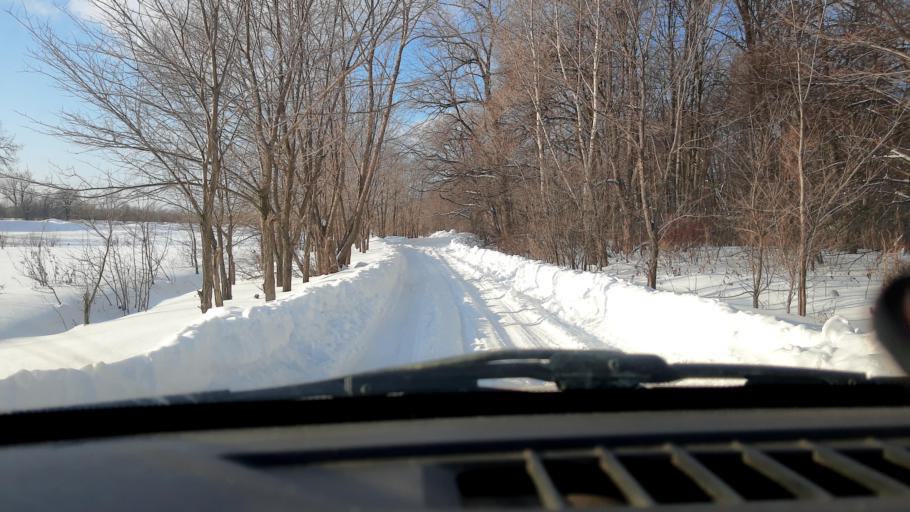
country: RU
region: Bashkortostan
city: Ufa
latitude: 54.6323
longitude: 56.0067
